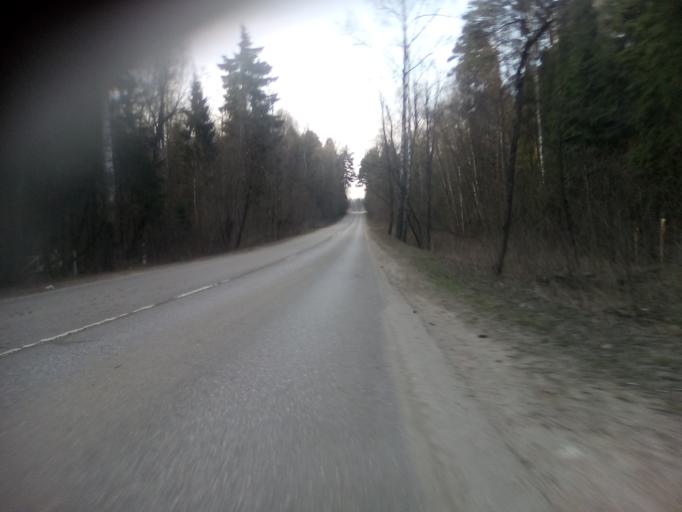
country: RU
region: Moskovskaya
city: Dubrovitsy
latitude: 55.4375
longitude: 37.3989
